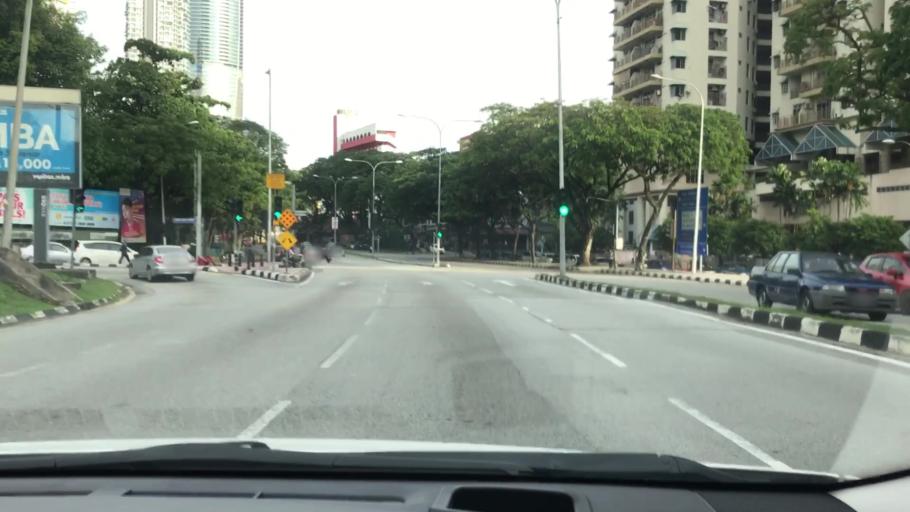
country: MY
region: Kuala Lumpur
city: Kuala Lumpur
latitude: 3.1172
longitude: 101.6677
